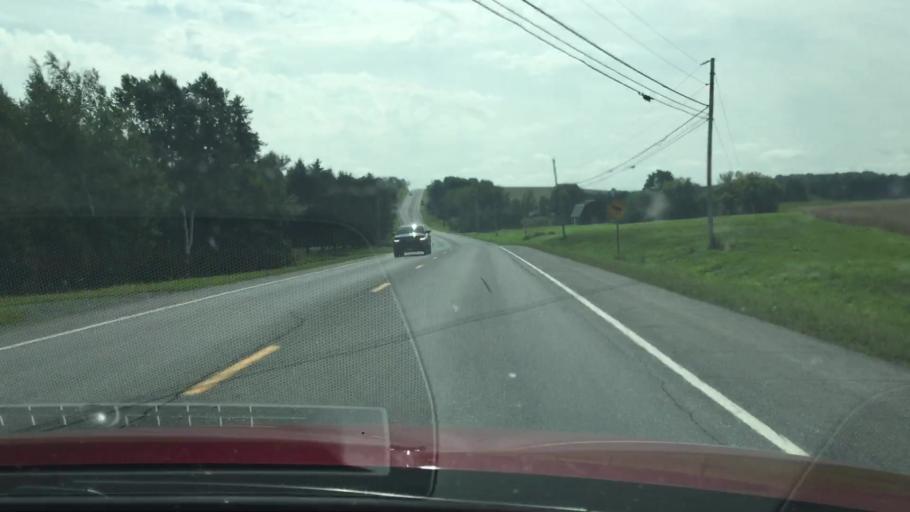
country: US
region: Maine
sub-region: Aroostook County
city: Easton
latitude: 46.5861
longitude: -67.9606
